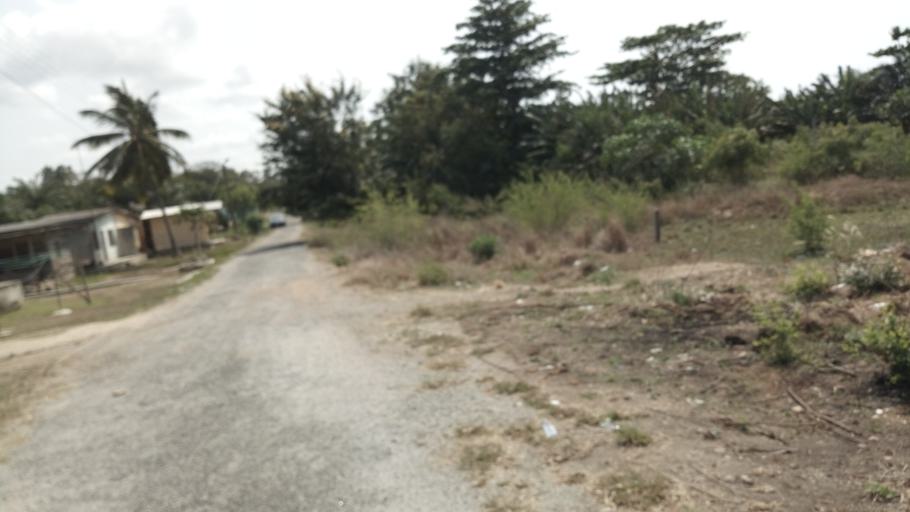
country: GH
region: Central
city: Winneba
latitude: 5.3690
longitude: -0.6425
